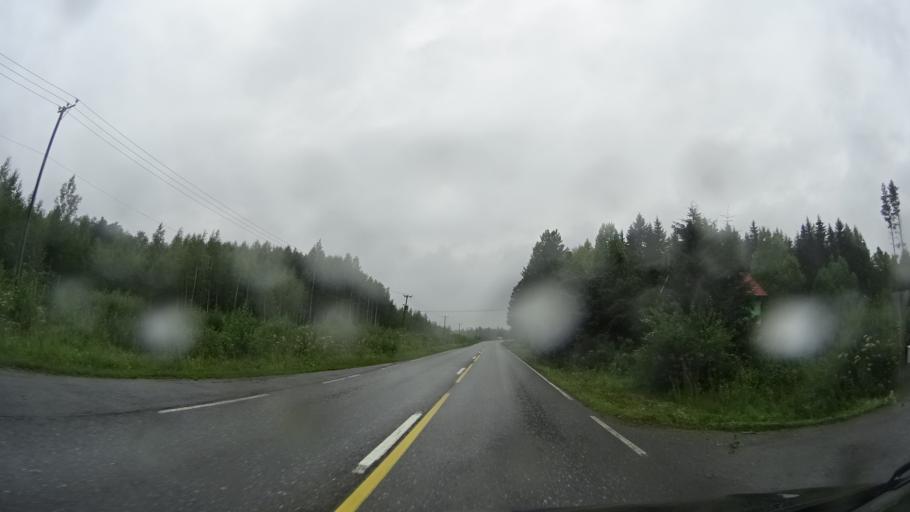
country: FI
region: North Karelia
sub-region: Keski-Karjala
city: Raeaekkylae
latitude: 62.3104
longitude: 29.5240
